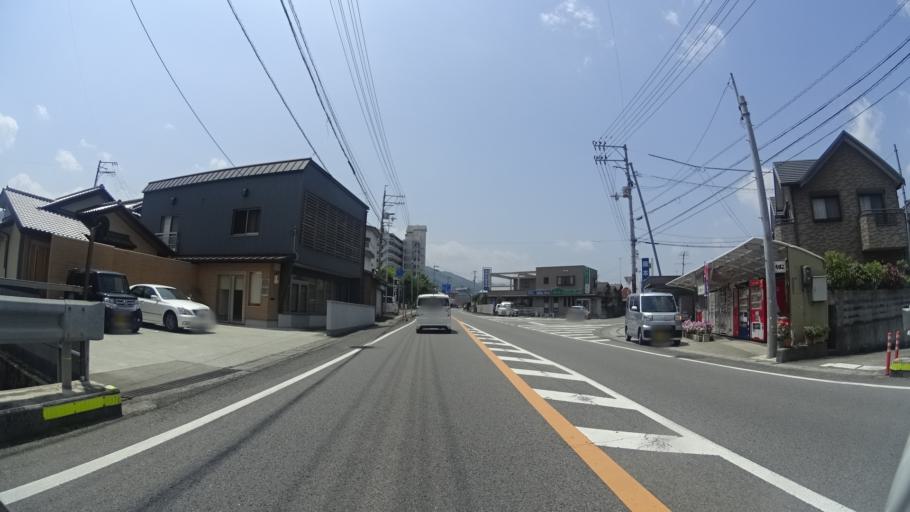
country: JP
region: Tokushima
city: Kamojimacho-jogejima
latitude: 34.0665
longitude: 134.3291
